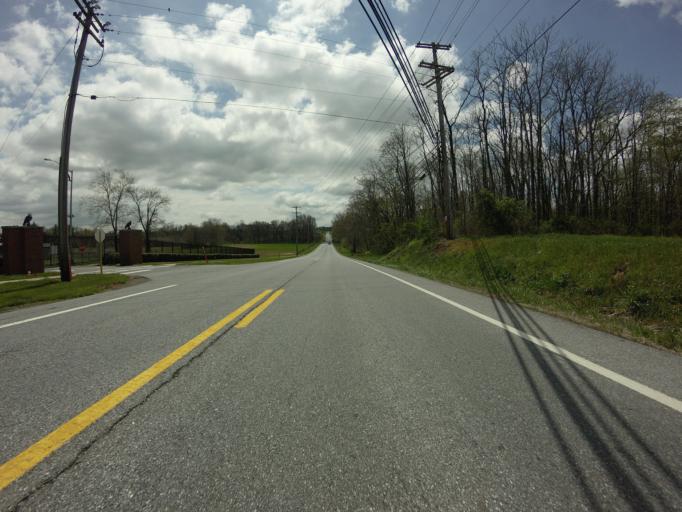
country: US
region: Maryland
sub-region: Frederick County
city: Emmitsburg
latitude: 39.6943
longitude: -77.3313
